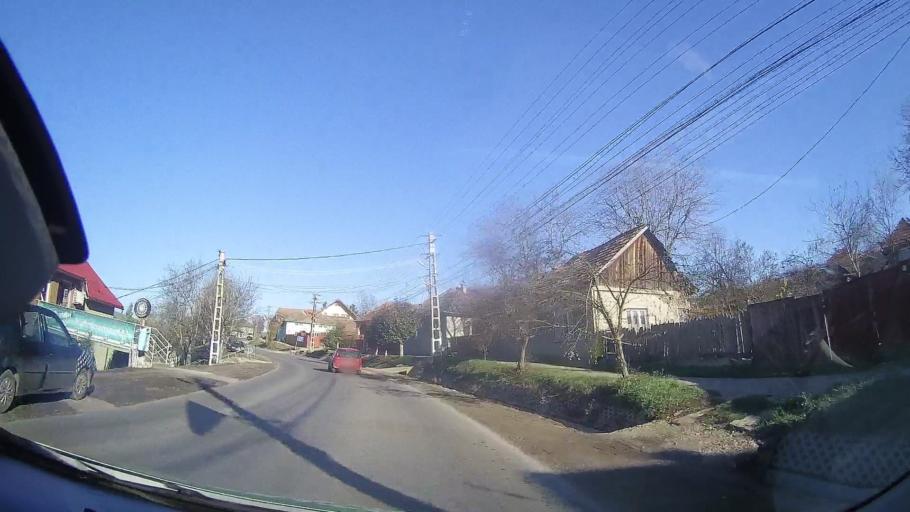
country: RO
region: Mures
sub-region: Comuna Sarmasu
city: Sarmasu
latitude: 46.7487
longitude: 24.1534
